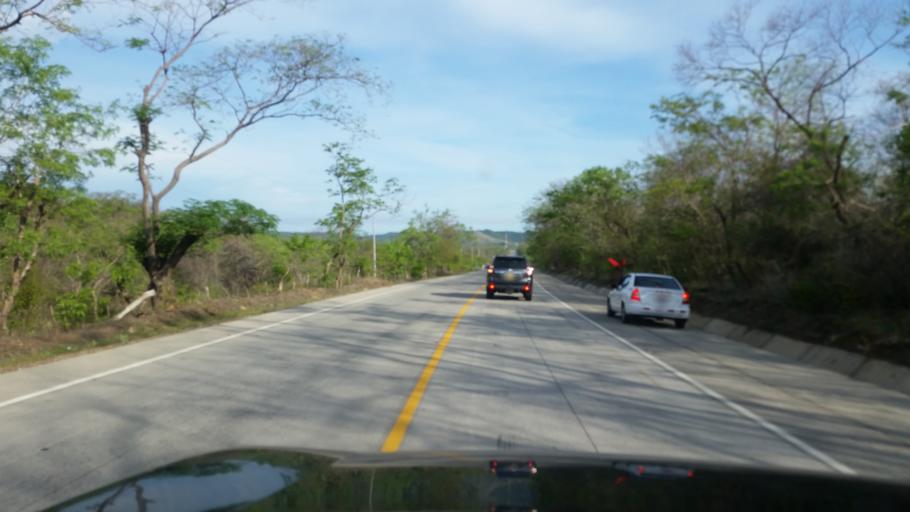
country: NI
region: Leon
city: Nagarote
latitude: 12.1210
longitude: -86.6270
